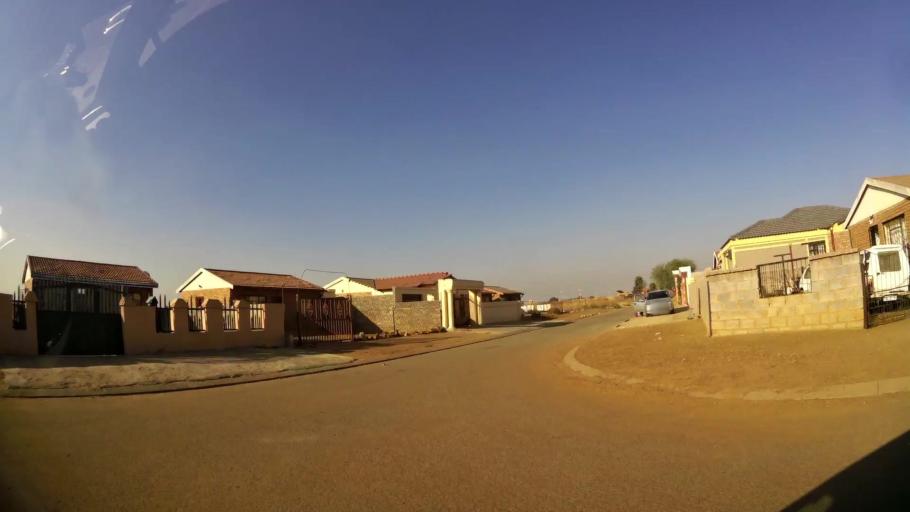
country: ZA
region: Gauteng
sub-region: West Rand District Municipality
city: Randfontein
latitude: -26.1975
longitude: 27.7021
